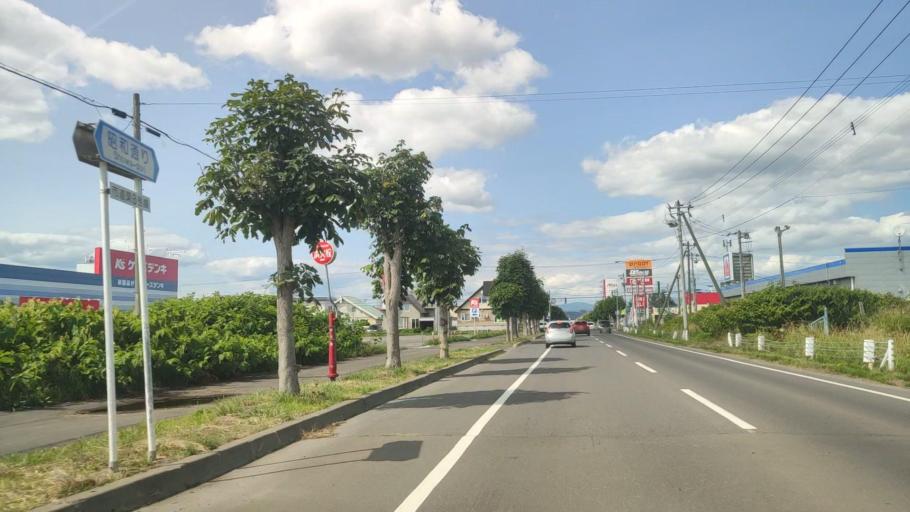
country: JP
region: Hokkaido
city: Nayoro
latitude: 44.3354
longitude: 142.4503
